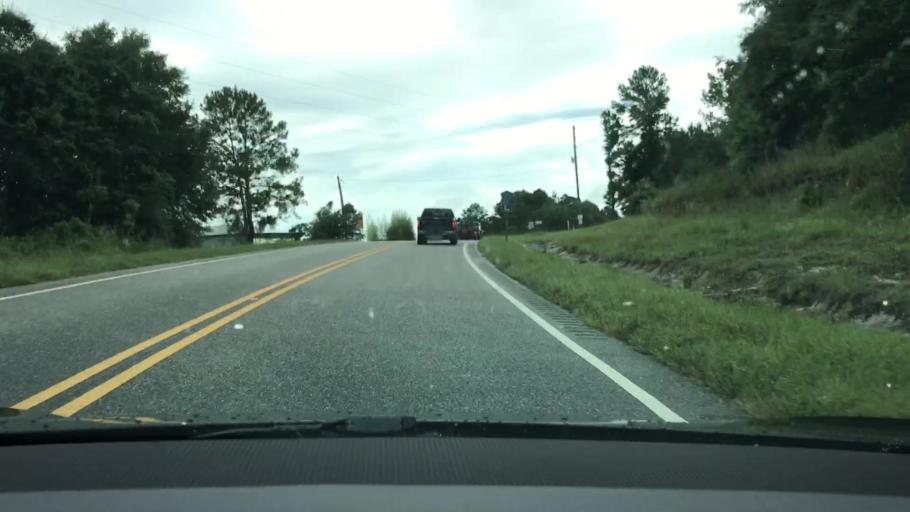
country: US
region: Alabama
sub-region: Geneva County
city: Samson
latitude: 31.0413
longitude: -86.1016
